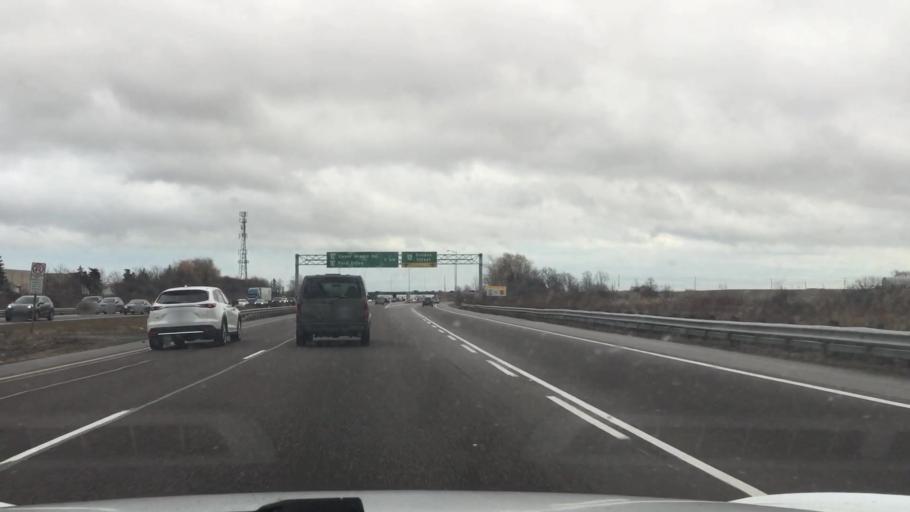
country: CA
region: Ontario
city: Oakville
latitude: 43.5155
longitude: -79.7015
